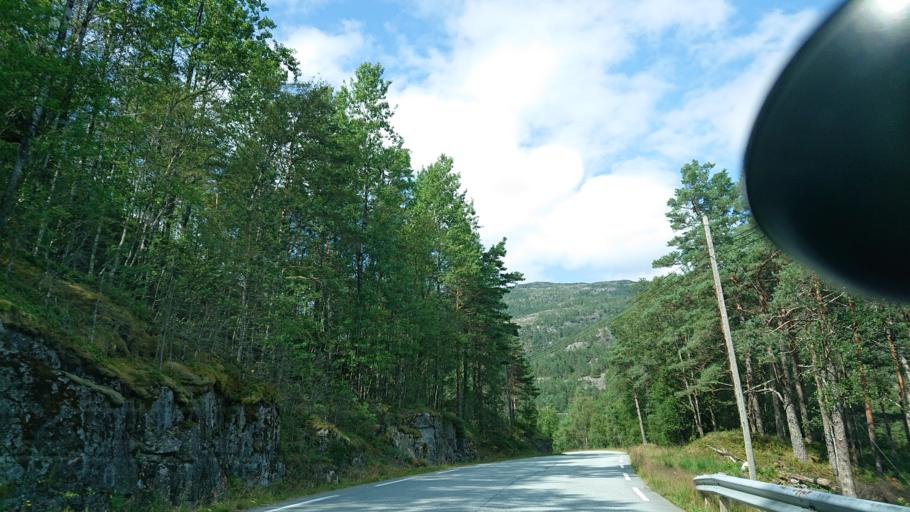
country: NO
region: Rogaland
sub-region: Hjelmeland
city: Hjelmelandsvagen
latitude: 59.2423
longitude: 6.2840
